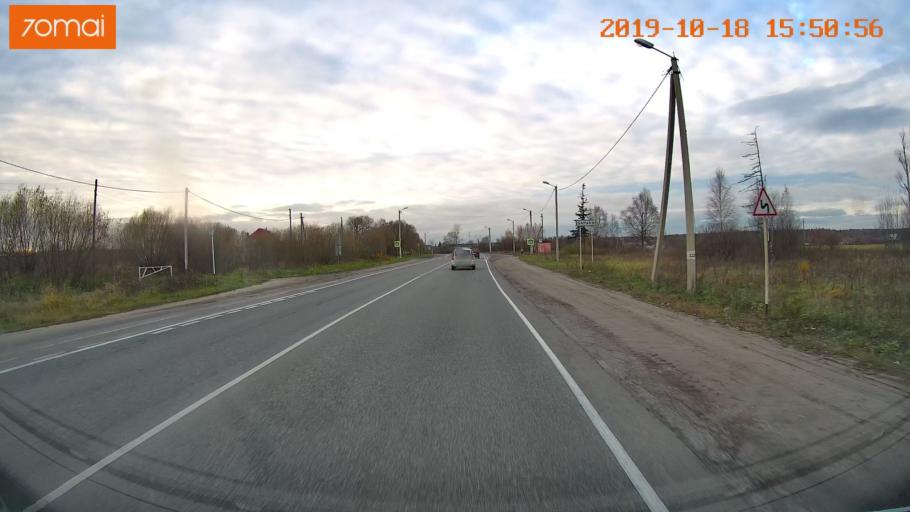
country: RU
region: Vladimir
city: Kommunar
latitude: 56.0374
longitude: 40.5536
